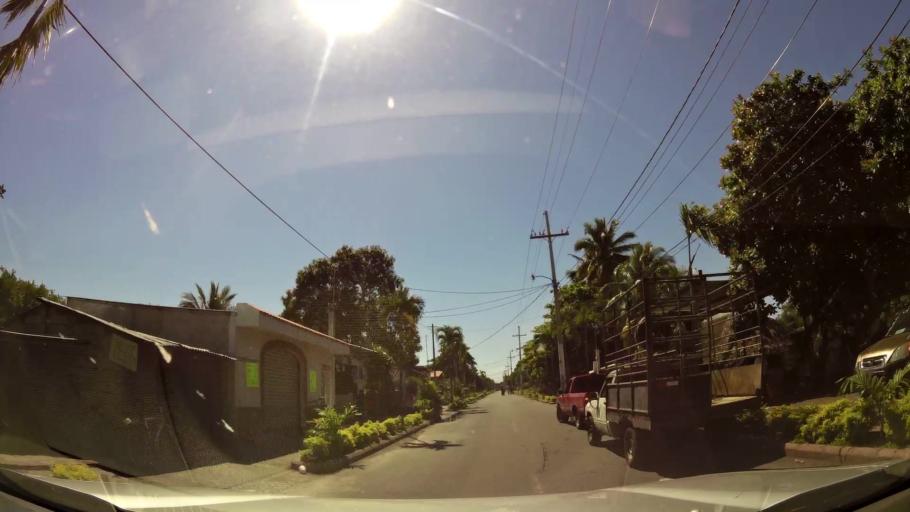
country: GT
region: Escuintla
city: Iztapa
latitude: 13.9345
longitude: -90.7146
